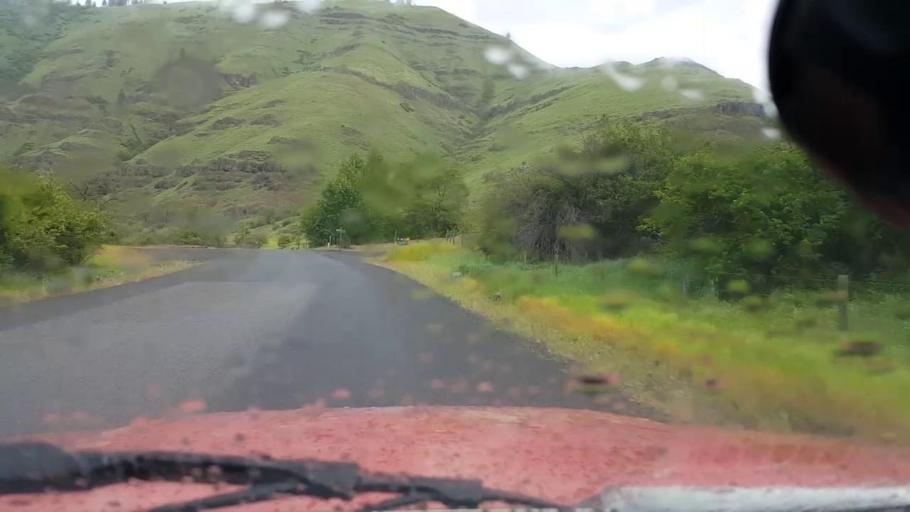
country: US
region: Washington
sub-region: Asotin County
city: Asotin
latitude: 46.0322
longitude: -117.3182
